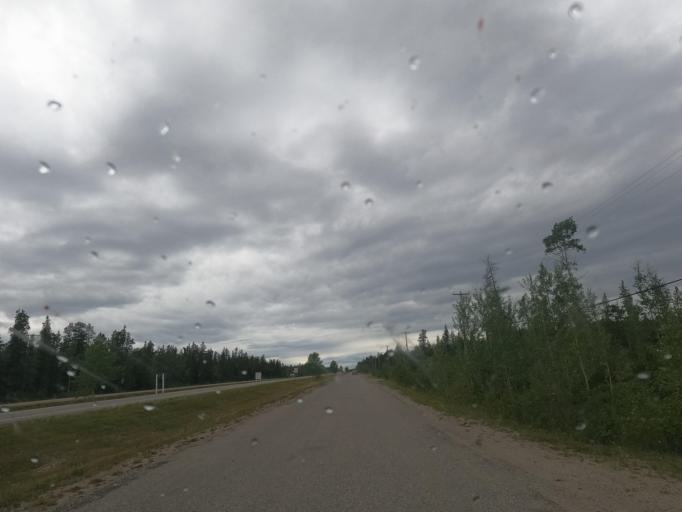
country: CA
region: Yukon
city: Watson Lake
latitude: 60.0509
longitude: -128.6578
